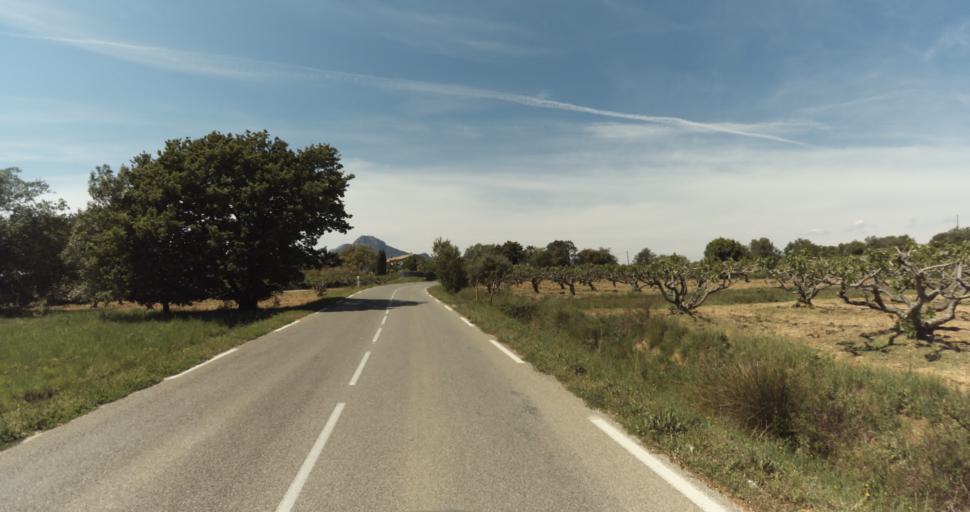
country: FR
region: Provence-Alpes-Cote d'Azur
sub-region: Departement du Var
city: La Crau
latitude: 43.1334
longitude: 6.0774
